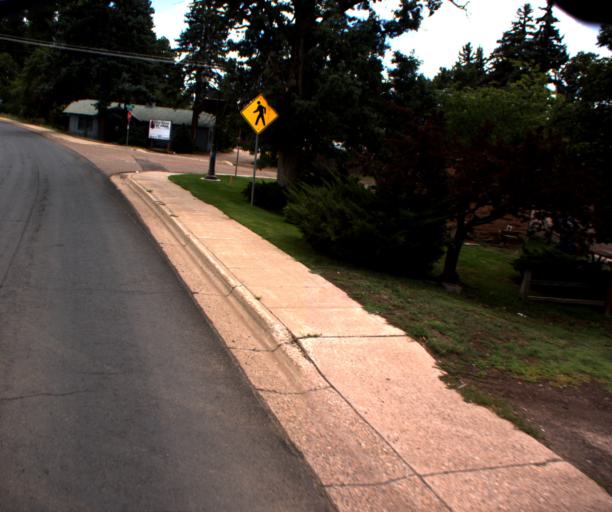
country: US
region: Arizona
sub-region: Navajo County
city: Pinetop-Lakeside
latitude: 34.1494
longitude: -109.9732
